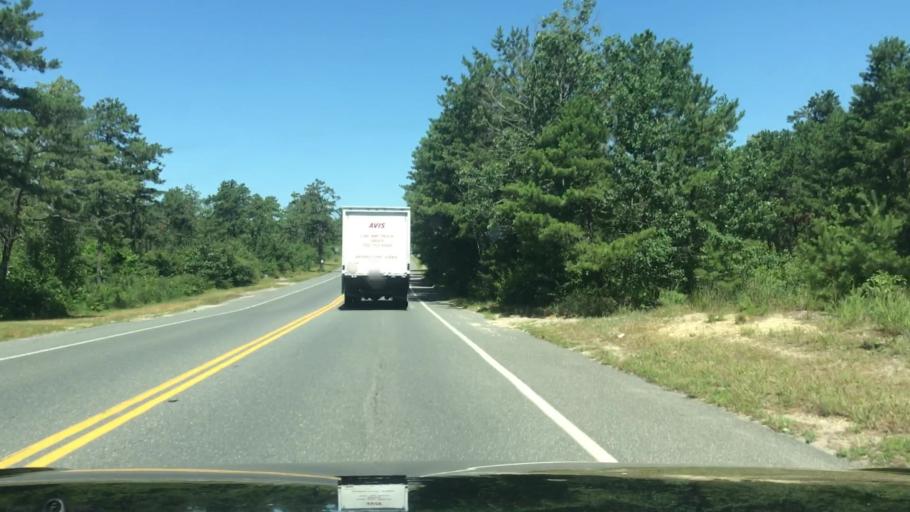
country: US
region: New Jersey
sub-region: Ocean County
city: Holiday City South
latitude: 39.9400
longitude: -74.2349
